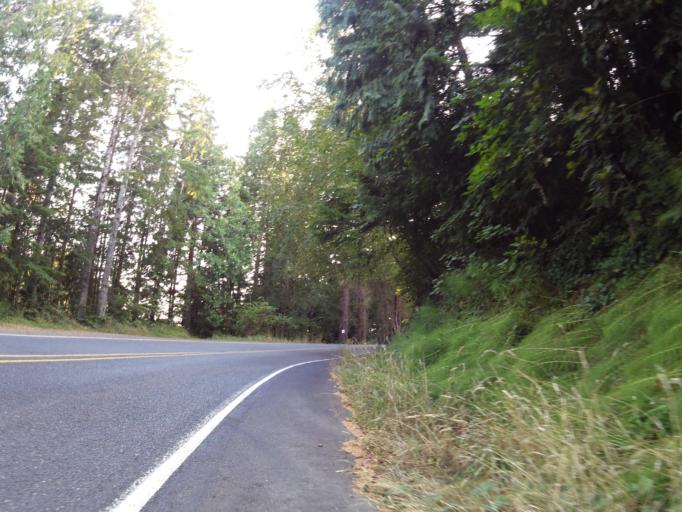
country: US
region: Oregon
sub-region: Lincoln County
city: Lincoln City
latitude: 44.9613
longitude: -124.0056
